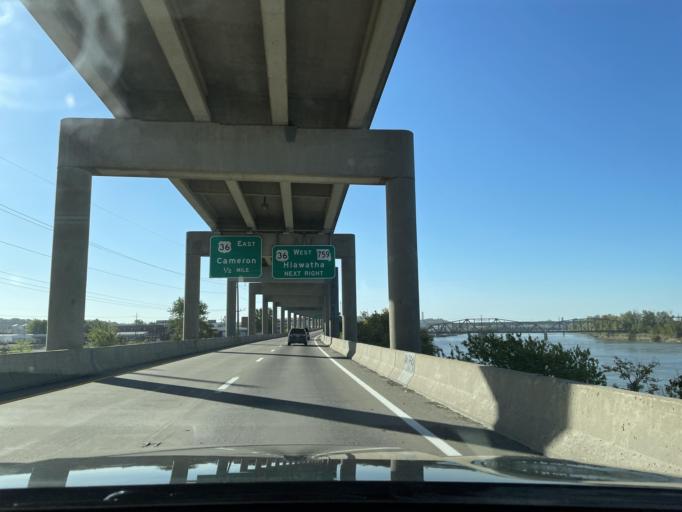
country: US
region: Missouri
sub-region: Buchanan County
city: Saint Joseph
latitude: 39.7586
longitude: -94.8569
